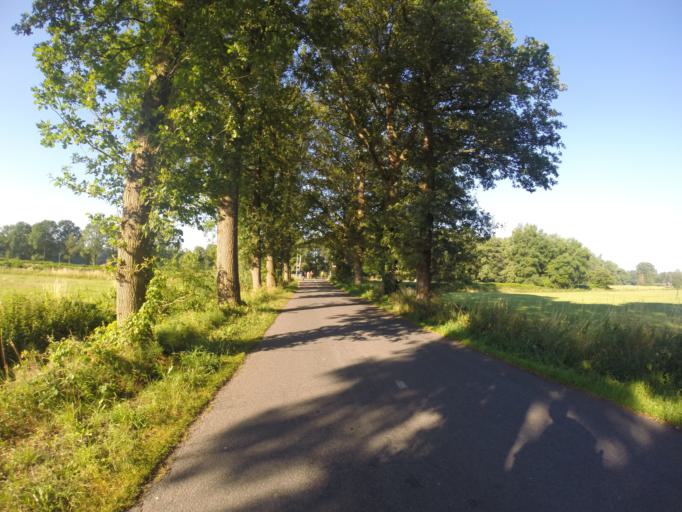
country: NL
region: Gelderland
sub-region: Gemeente Lochem
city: Barchem
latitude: 52.0938
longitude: 6.3836
